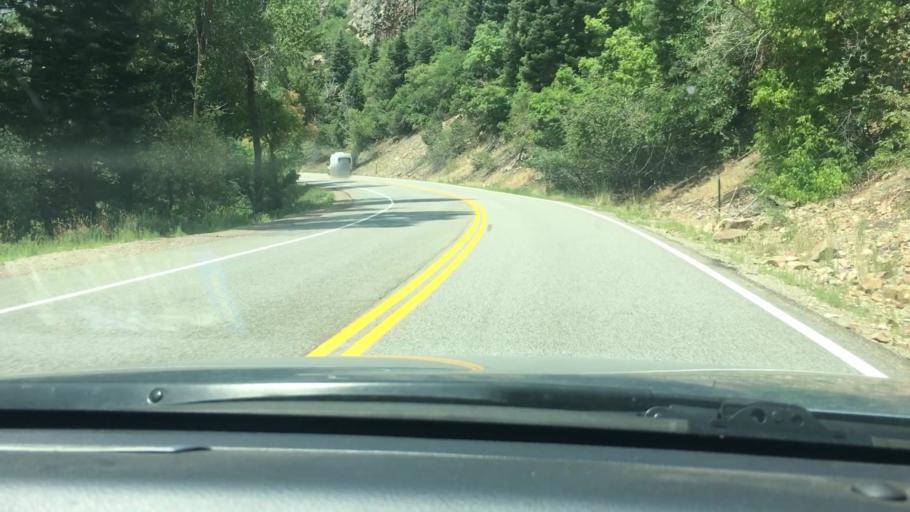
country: US
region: Utah
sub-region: Salt Lake County
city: Mount Olympus
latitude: 40.6350
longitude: -111.7289
